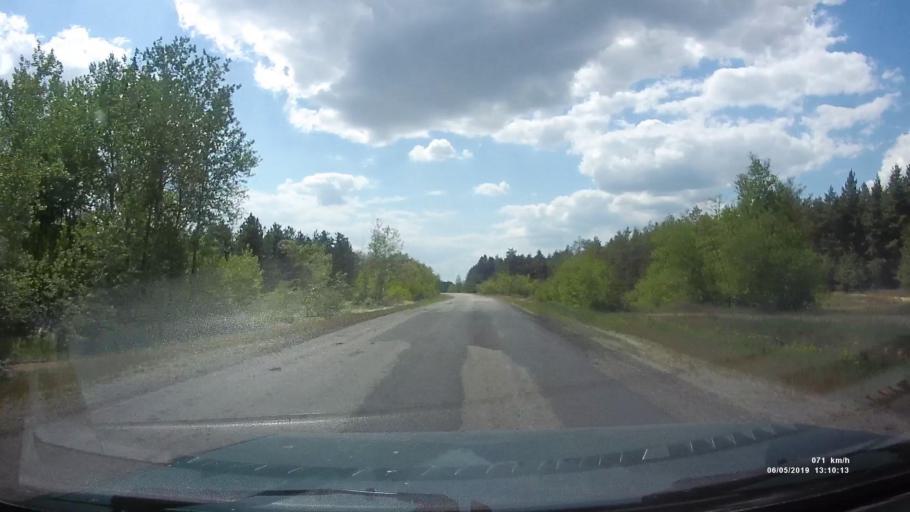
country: RU
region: Rostov
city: Ust'-Donetskiy
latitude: 47.7626
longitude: 40.9742
